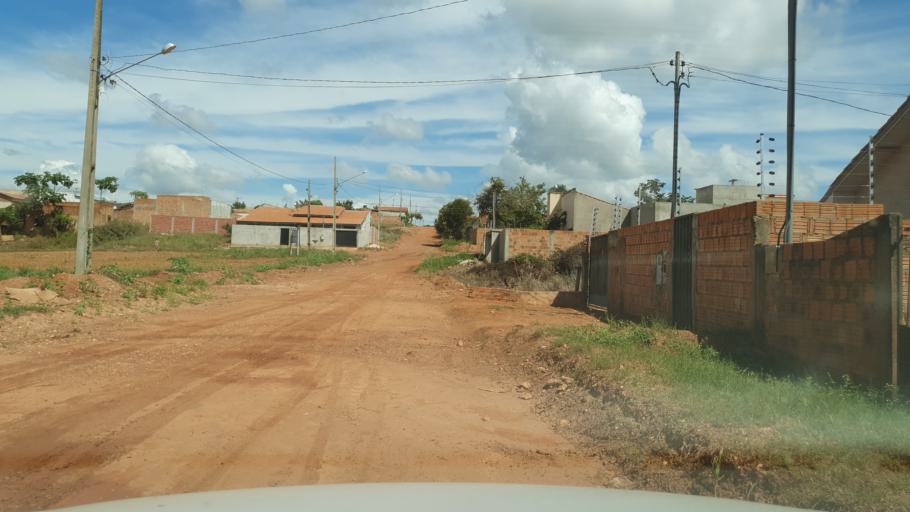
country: BR
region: Mato Grosso
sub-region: Pontes E Lacerda
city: Pontes e Lacerda
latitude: -15.2514
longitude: -59.3127
